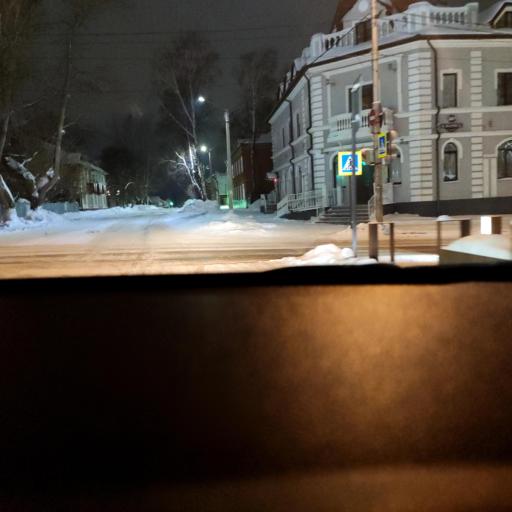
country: RU
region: Tatarstan
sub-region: Chistopol'skiy Rayon
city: Chistopol'
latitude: 55.3677
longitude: 50.6425
